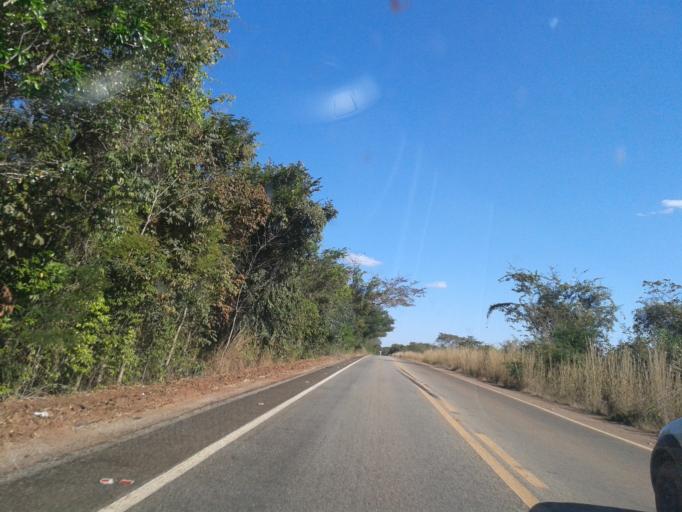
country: BR
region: Goias
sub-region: Mozarlandia
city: Mozarlandia
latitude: -14.4215
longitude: -50.4510
